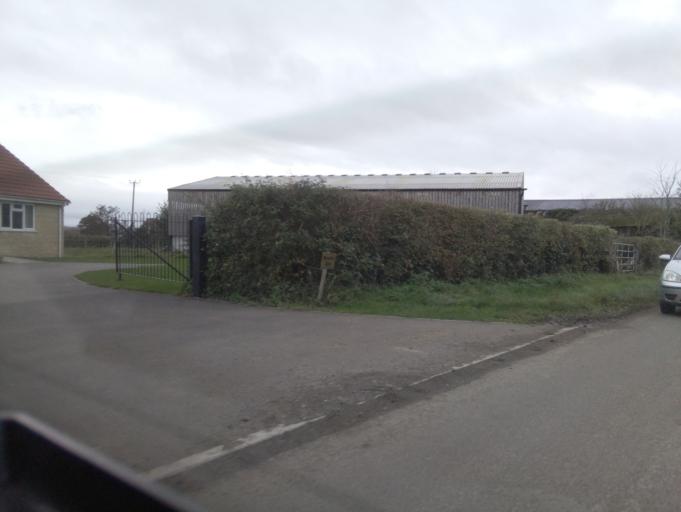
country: GB
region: England
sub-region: Somerset
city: Yeovil
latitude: 51.0020
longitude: -2.5914
